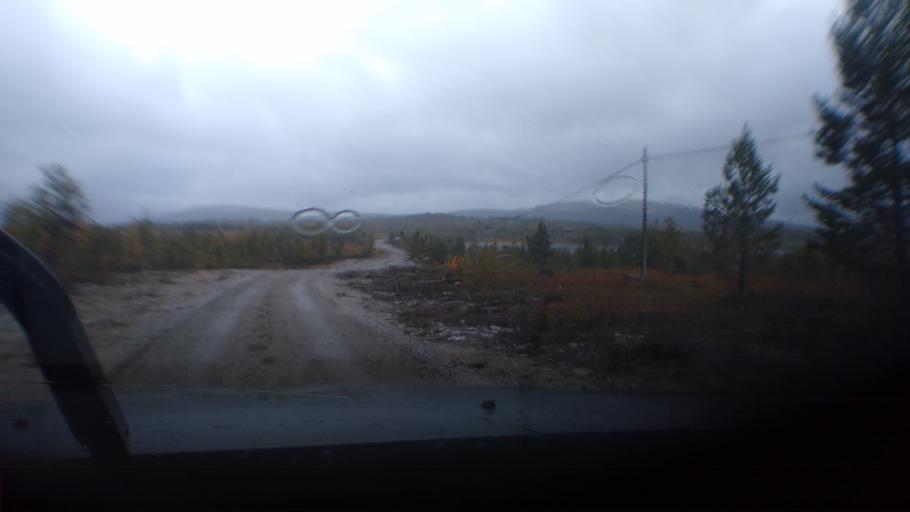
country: NO
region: Oppland
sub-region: Ringebu
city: Ringebu
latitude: 61.6604
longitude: 10.1040
